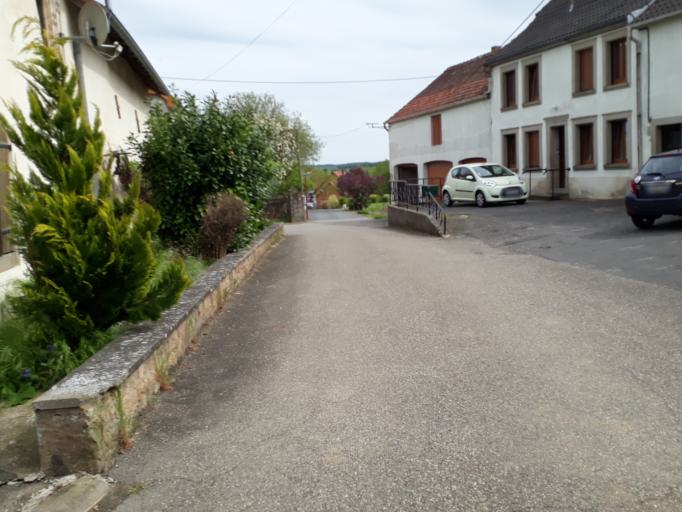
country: FR
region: Alsace
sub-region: Departement du Bas-Rhin
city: Diemeringen
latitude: 48.9102
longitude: 7.1456
